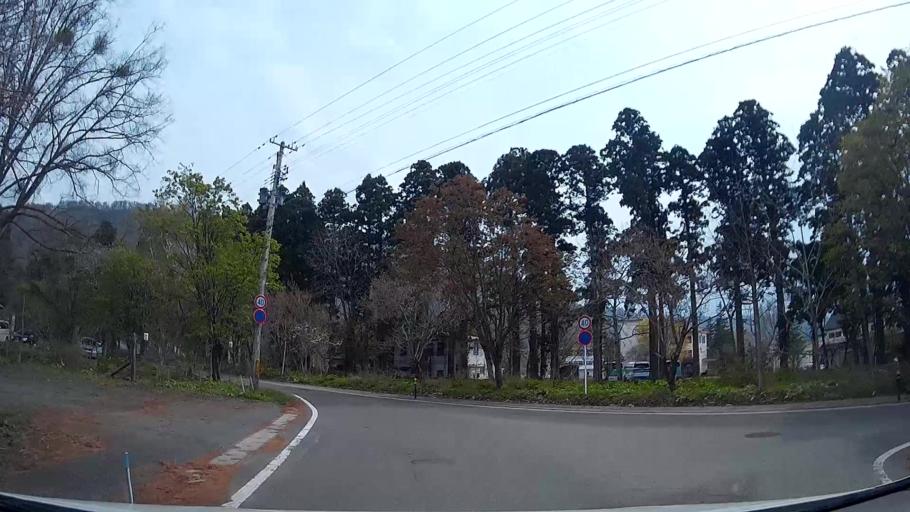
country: JP
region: Akita
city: Hanawa
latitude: 40.4270
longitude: 140.8953
